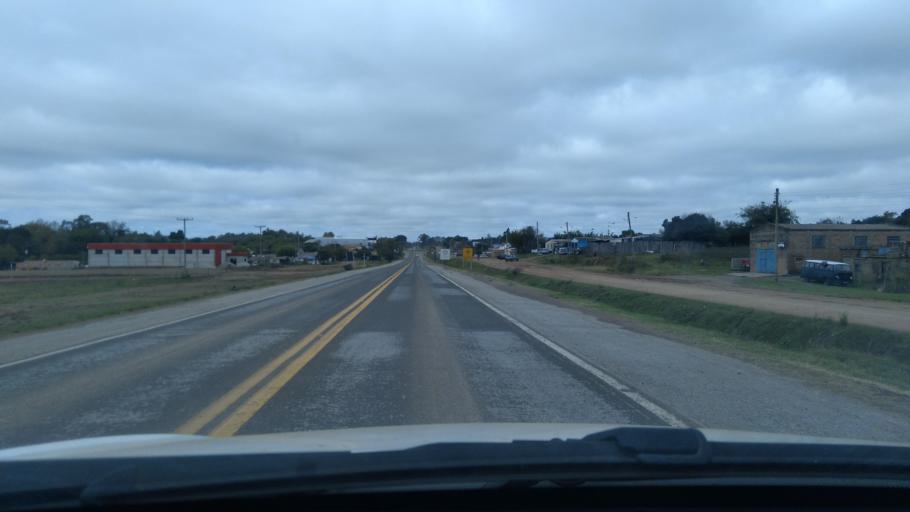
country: BR
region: Rio Grande do Sul
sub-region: Dom Pedrito
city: Dom Pedrito
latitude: -30.9647
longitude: -54.6690
